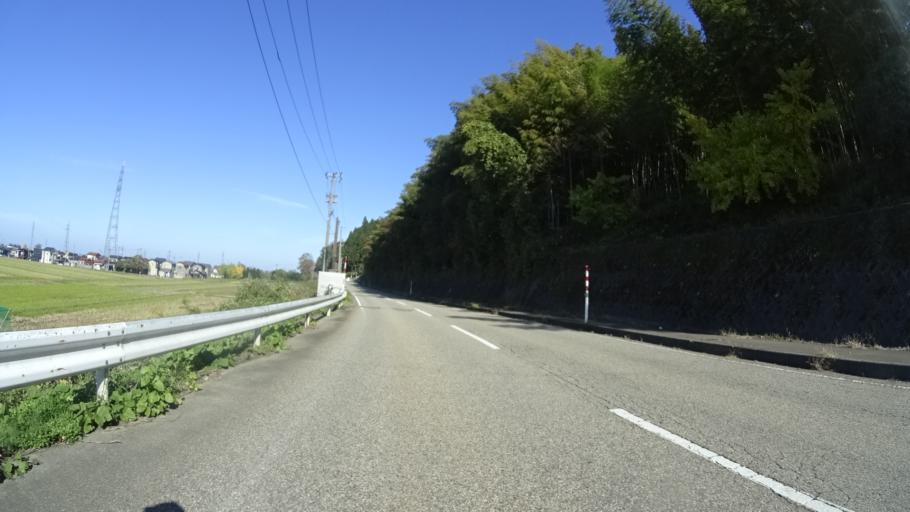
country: JP
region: Ishikawa
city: Tsurugi-asahimachi
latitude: 36.4787
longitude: 136.6161
